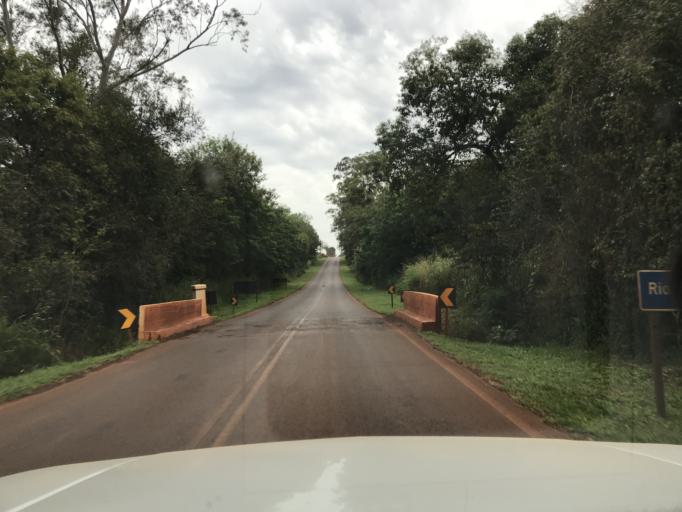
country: BR
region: Parana
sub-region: Palotina
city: Palotina
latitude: -24.4309
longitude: -53.9104
